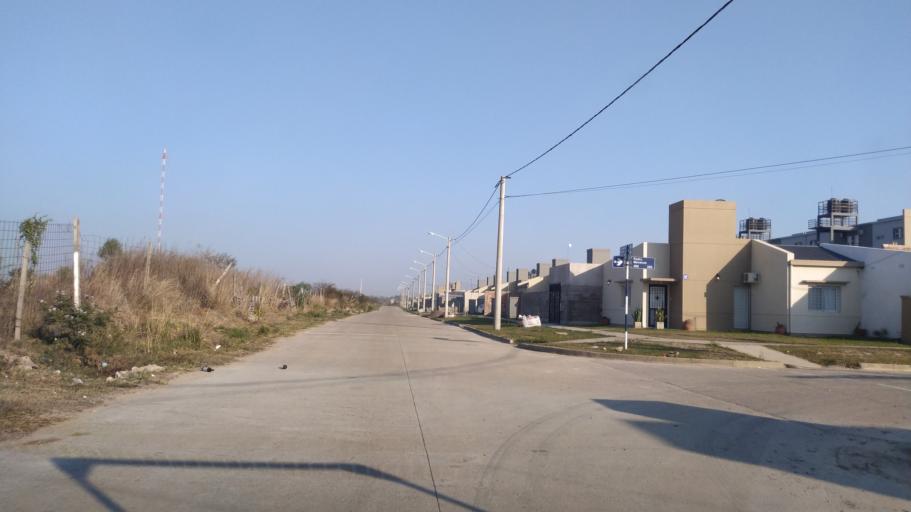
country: AR
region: Corrientes
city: Corrientes
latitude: -27.5284
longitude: -58.8050
